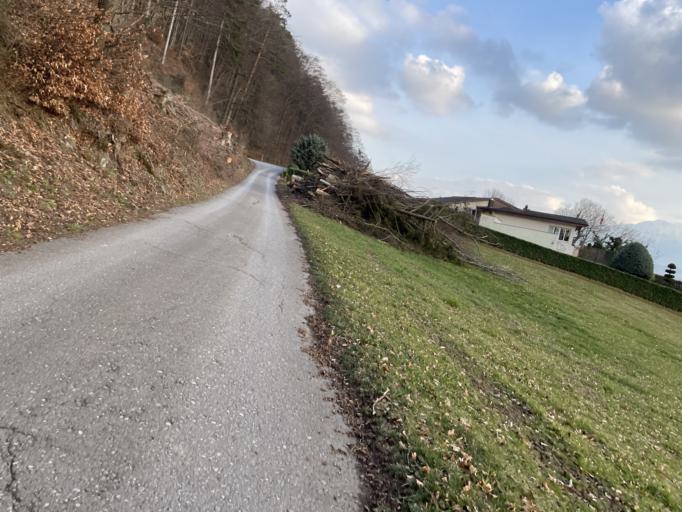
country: CH
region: Bern
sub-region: Bern-Mittelland District
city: Muhlethurnen
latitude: 46.8424
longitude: 7.5235
